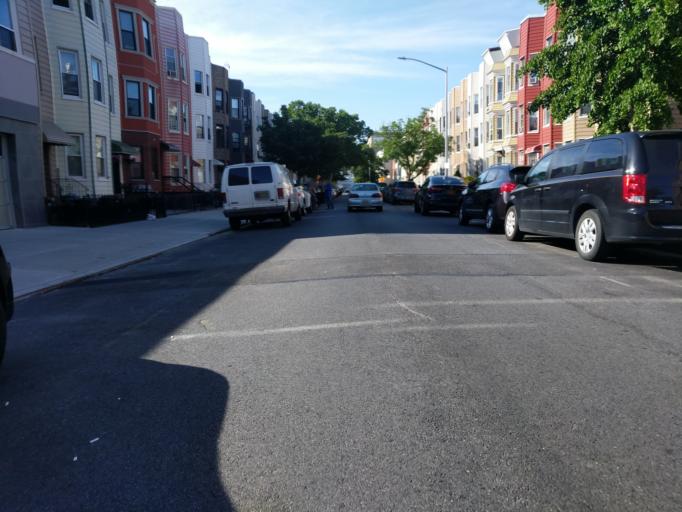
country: US
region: New York
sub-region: Queens County
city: Long Island City
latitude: 40.7257
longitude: -73.9445
